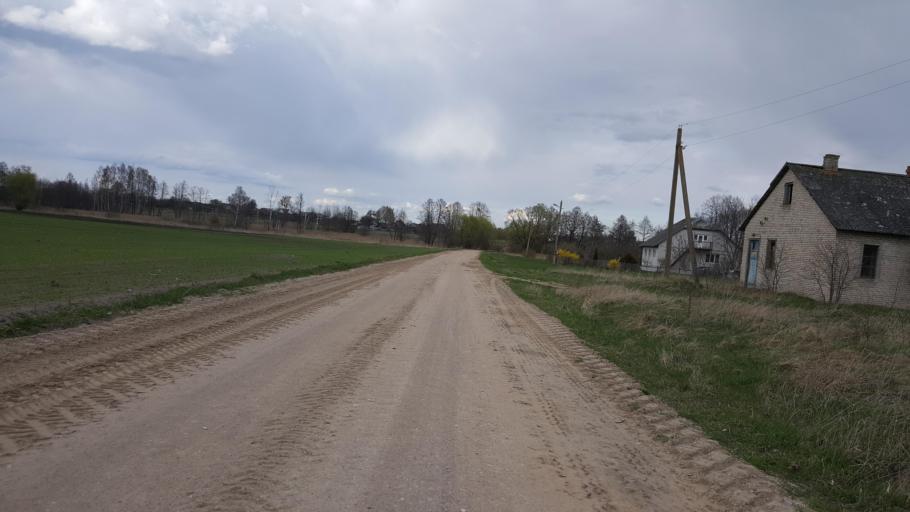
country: BY
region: Brest
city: Kamyanyets
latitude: 52.3944
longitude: 23.7540
